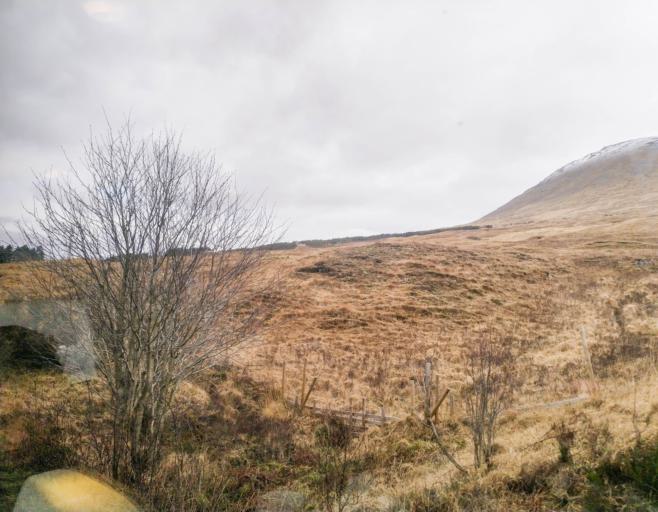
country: GB
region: Scotland
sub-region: Highland
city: Spean Bridge
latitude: 56.5143
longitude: -4.7627
